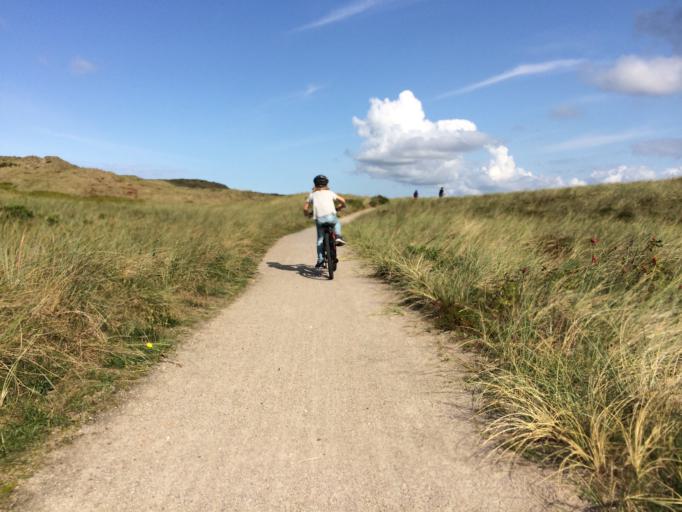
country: DK
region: Central Jutland
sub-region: Ringkobing-Skjern Kommune
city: Hvide Sande
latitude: 55.9397
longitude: 8.1492
